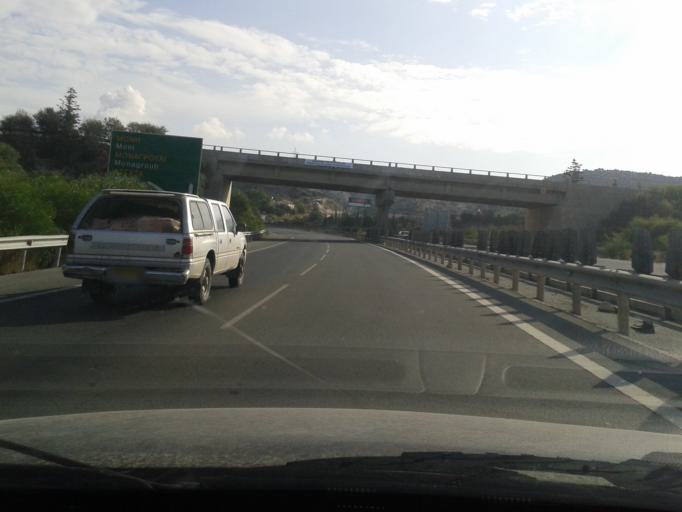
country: CY
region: Limassol
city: Pyrgos
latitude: 34.7219
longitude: 33.2019
